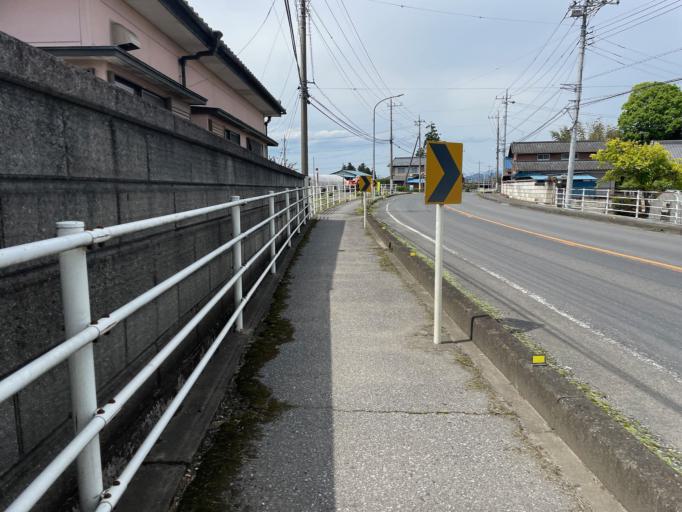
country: JP
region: Tochigi
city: Mibu
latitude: 36.4691
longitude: 139.7647
